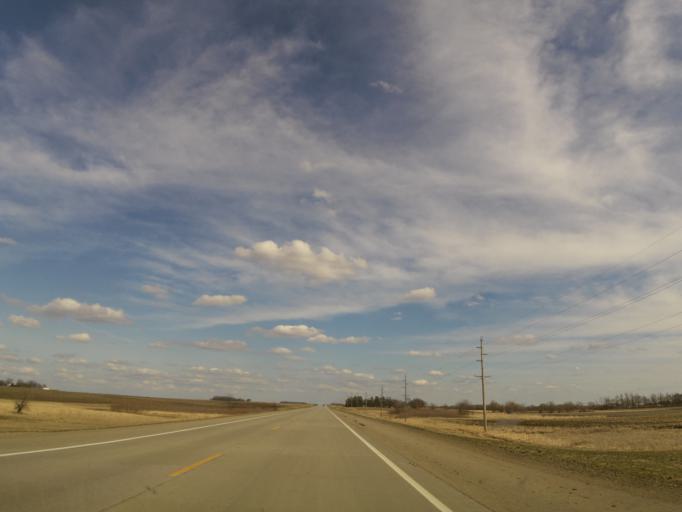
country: US
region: Minnesota
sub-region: Lac qui Parle County
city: Madison
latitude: 44.9358
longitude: -96.1453
